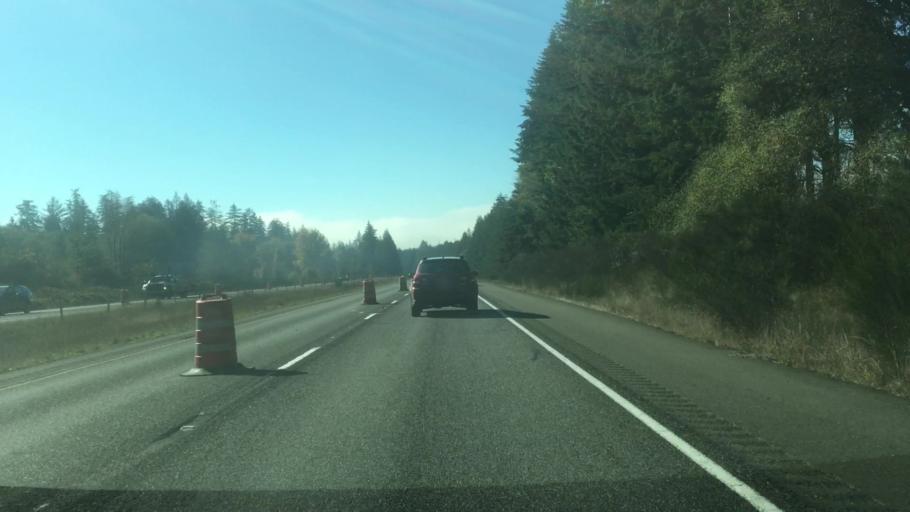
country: US
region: Washington
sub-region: Grays Harbor County
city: McCleary
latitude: 47.0509
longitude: -123.2998
